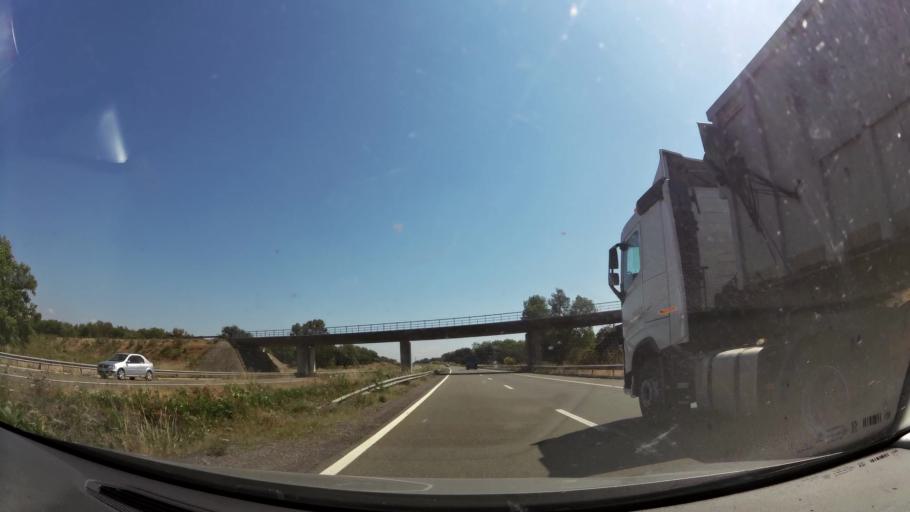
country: MA
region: Gharb-Chrarda-Beni Hssen
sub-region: Kenitra Province
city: Kenitra
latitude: 34.1573
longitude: -6.6767
